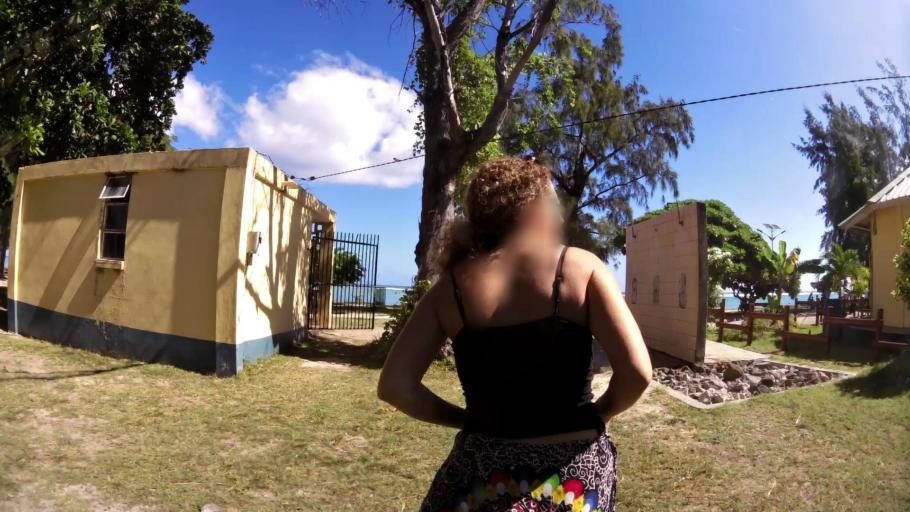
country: MU
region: Black River
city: Flic en Flac
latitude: -20.2857
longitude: 57.3641
